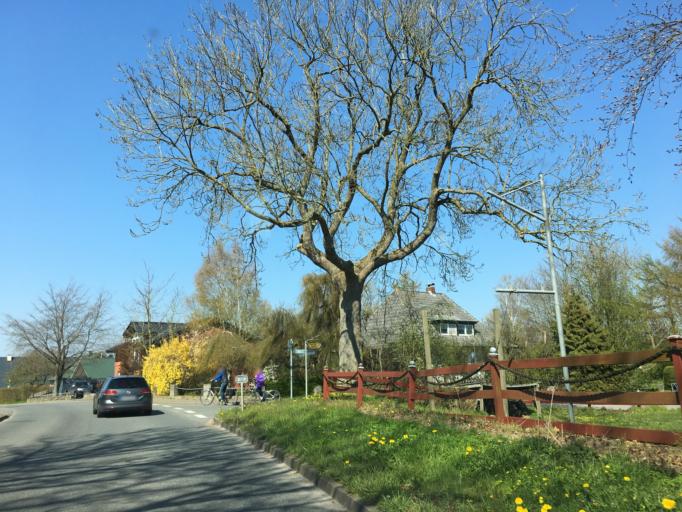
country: DE
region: Schleswig-Holstein
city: Dollrottfeld
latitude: 54.5924
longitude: 9.8034
